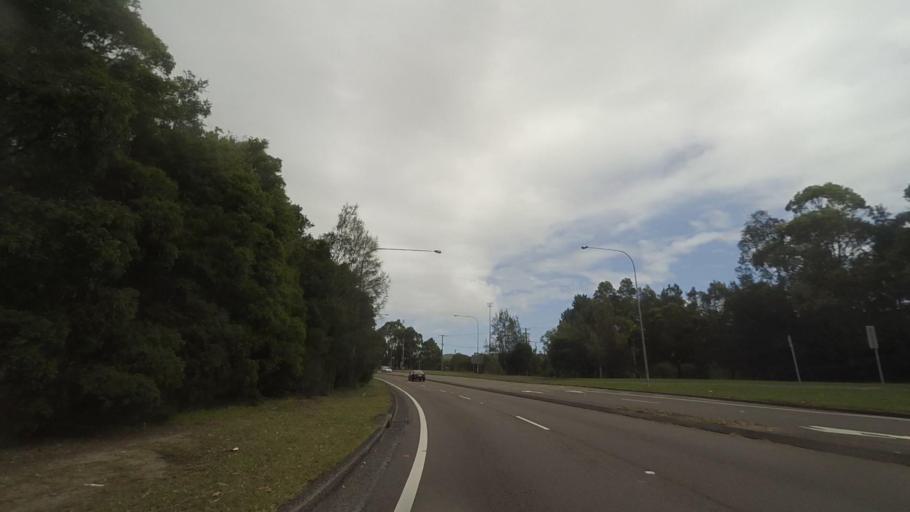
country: AU
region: New South Wales
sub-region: Wyong Shire
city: Berkeley Vale
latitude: -33.3575
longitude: 151.4401
